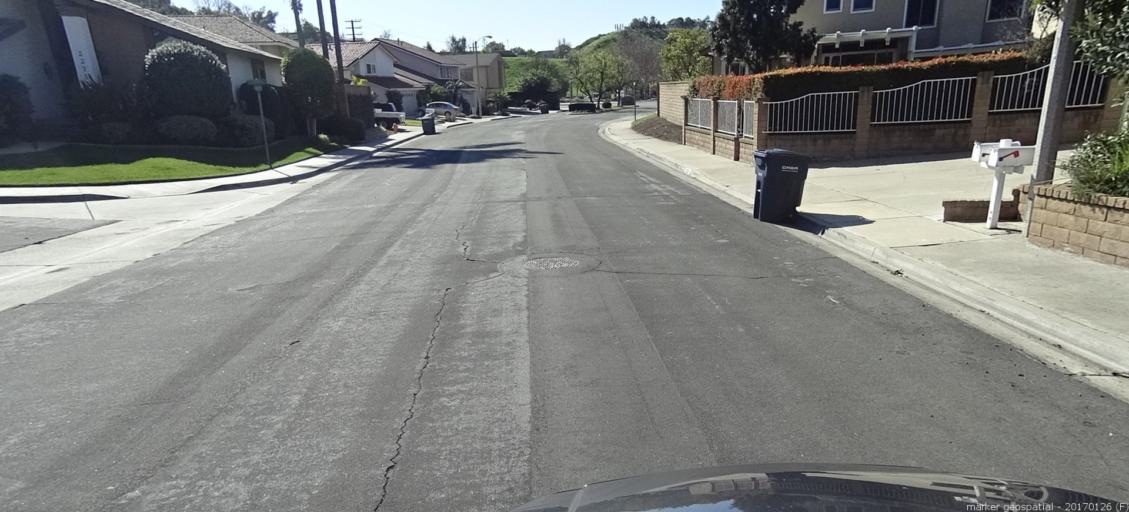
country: US
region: California
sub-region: Orange County
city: Lake Forest
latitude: 33.6330
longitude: -117.6749
